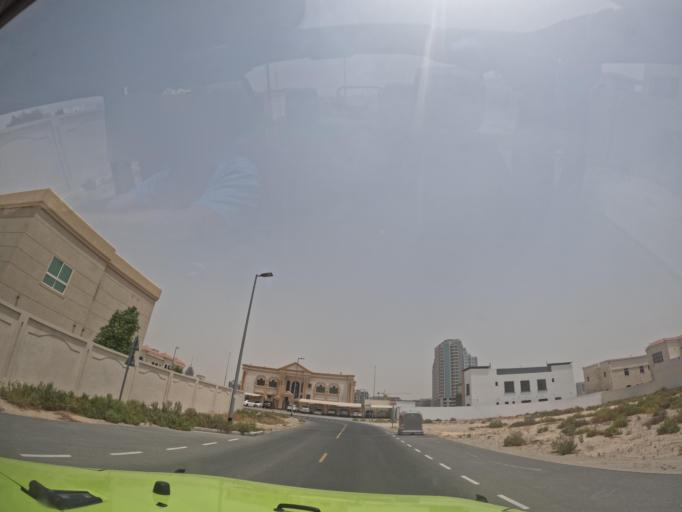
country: AE
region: Dubai
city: Dubai
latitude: 25.1268
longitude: 55.3707
